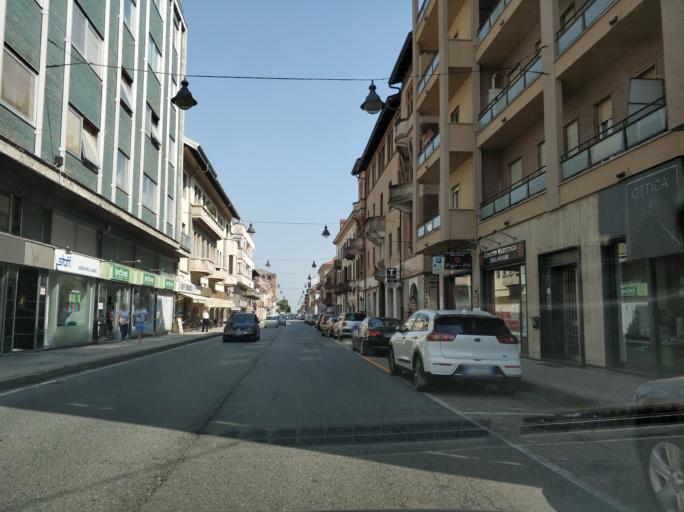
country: IT
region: Piedmont
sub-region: Provincia di Torino
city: Cuorgne
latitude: 45.3902
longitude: 7.6518
